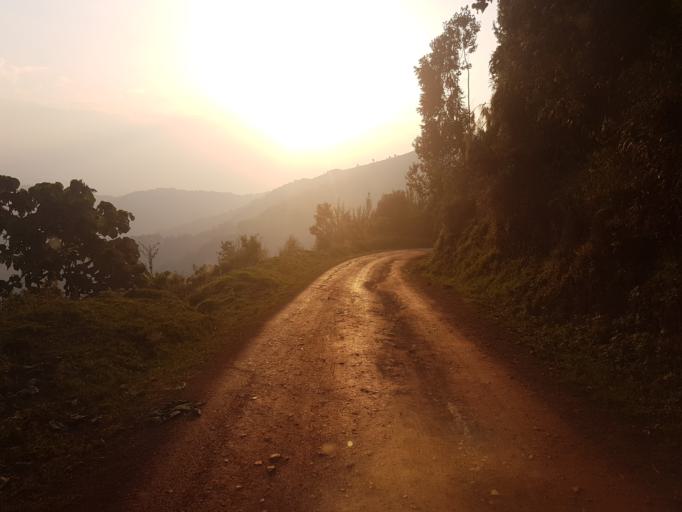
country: UG
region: Western Region
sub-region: Kanungu District
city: Kanungu
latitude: -1.0096
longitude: 29.8486
